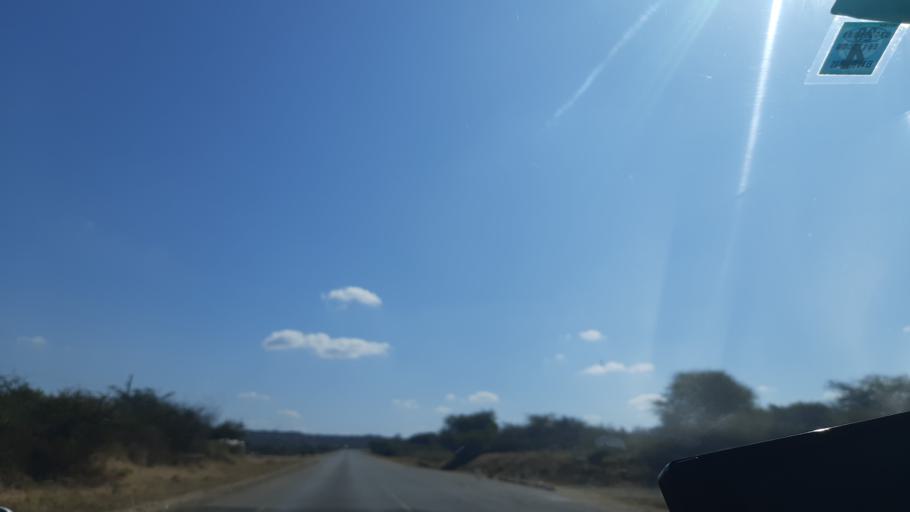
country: TZ
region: Singida
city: Kilimatinde
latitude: -5.7824
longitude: 34.8918
